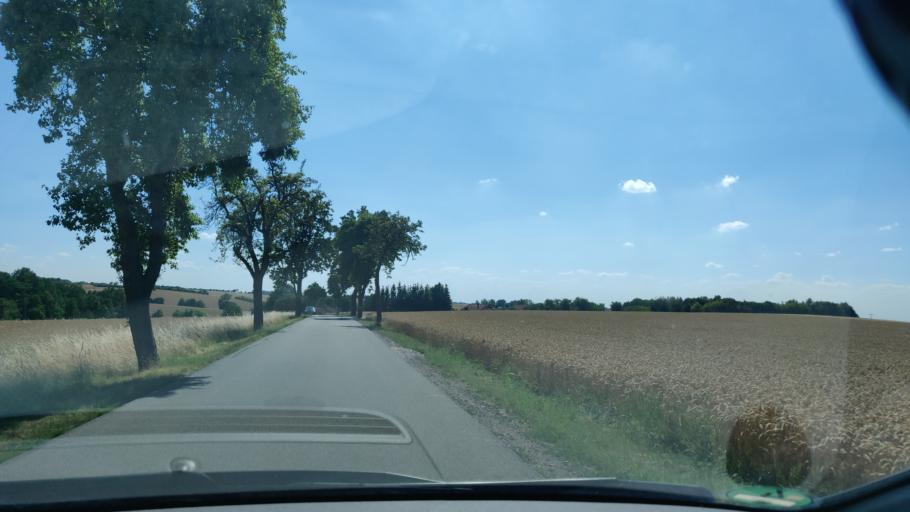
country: DE
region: Saxony
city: Geithain
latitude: 51.0590
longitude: 12.6646
